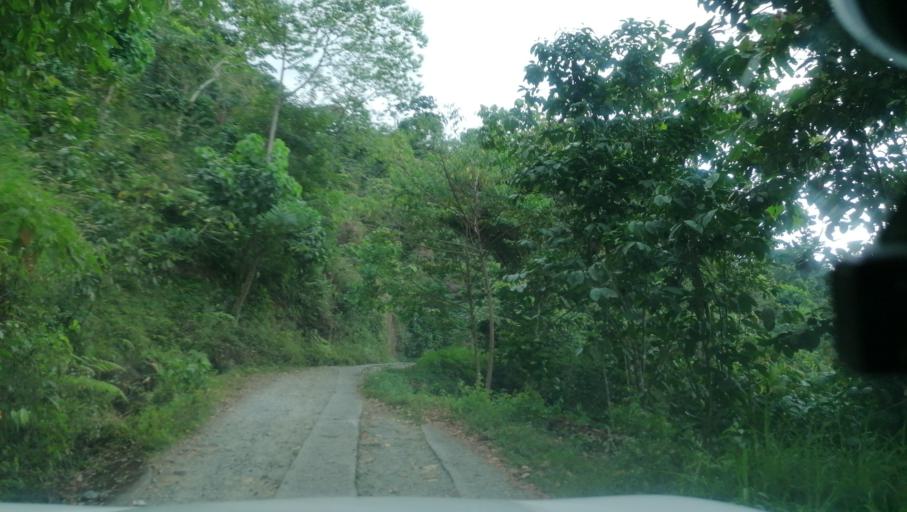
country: MX
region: Chiapas
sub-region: Cacahoatan
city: Benito Juarez
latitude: 15.0961
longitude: -92.1891
